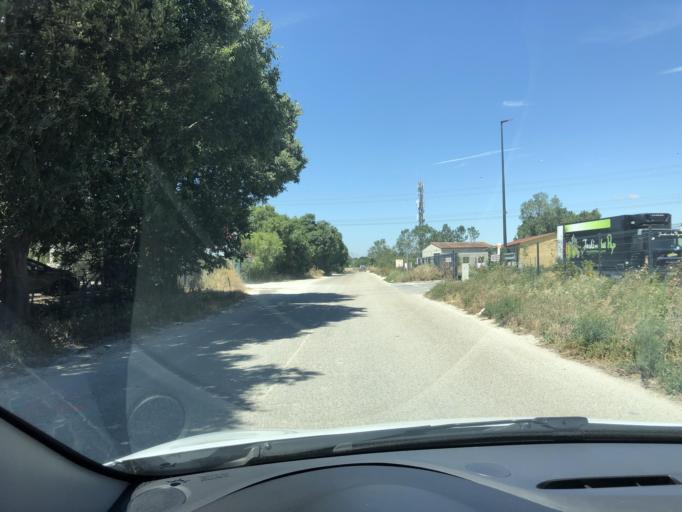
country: FR
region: Provence-Alpes-Cote d'Azur
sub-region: Departement des Bouches-du-Rhone
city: Chateaurenard
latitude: 43.8998
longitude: 4.8748
